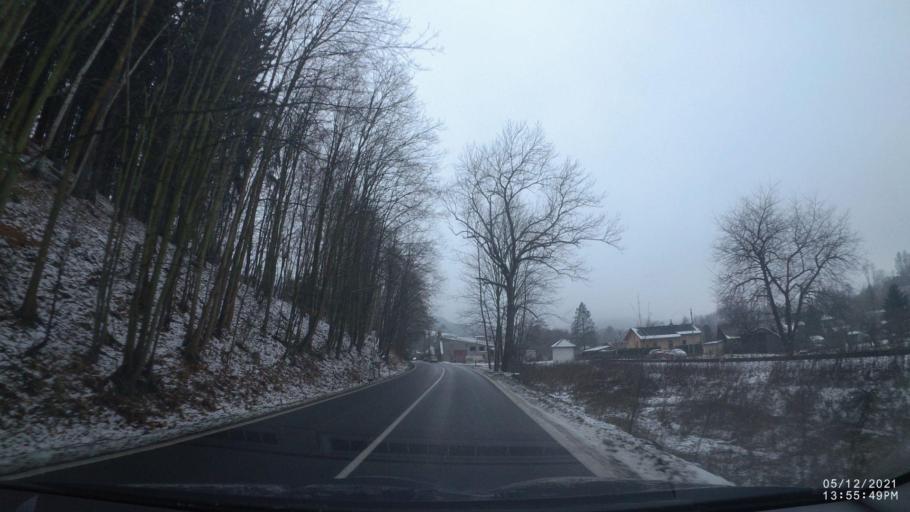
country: CZ
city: Hronov
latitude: 50.4961
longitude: 16.1965
